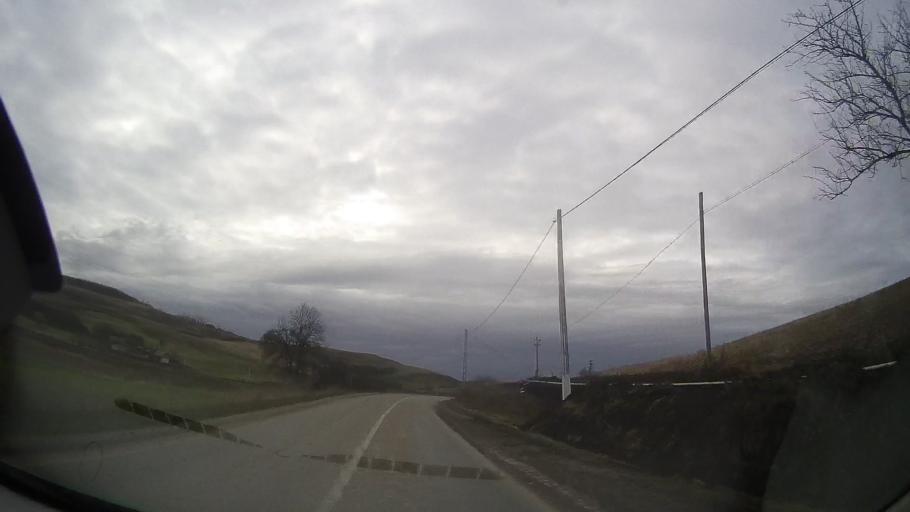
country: RO
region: Bistrita-Nasaud
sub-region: Comuna Budesti
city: Budesti
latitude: 46.8527
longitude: 24.2429
